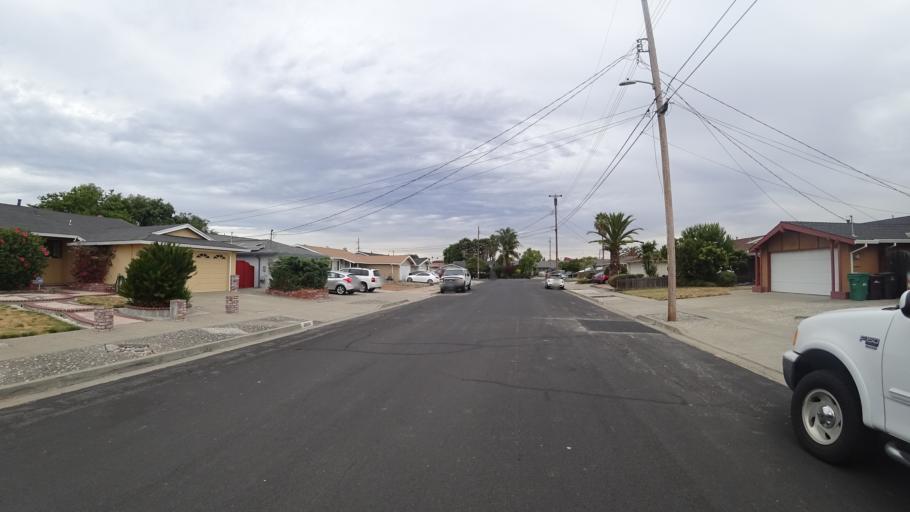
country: US
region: California
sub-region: Alameda County
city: Hayward
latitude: 37.6204
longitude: -122.0826
